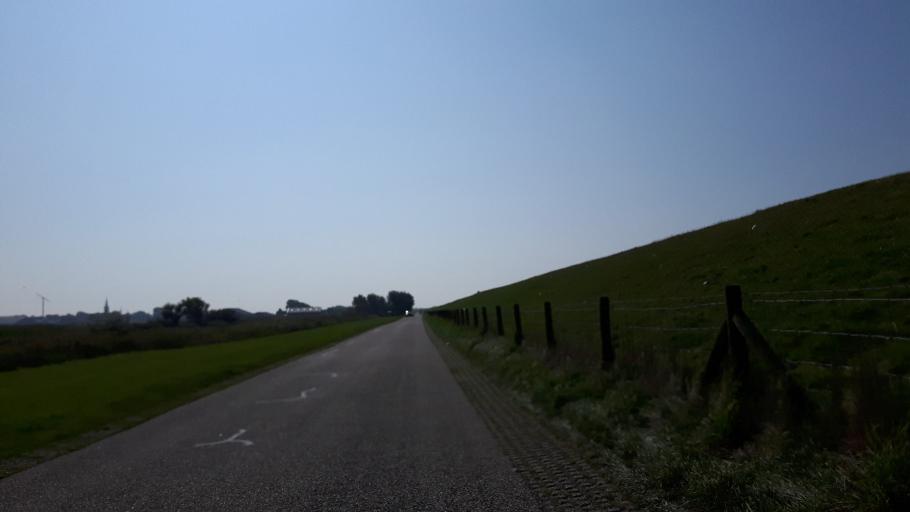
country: NL
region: Friesland
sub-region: Sudwest Fryslan
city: Makkum
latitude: 53.0911
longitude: 5.3802
